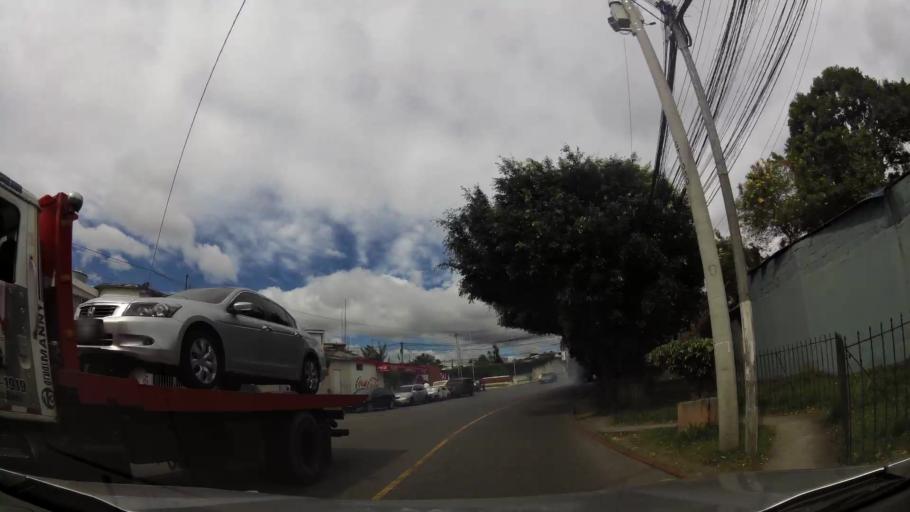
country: GT
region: Guatemala
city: Santa Catarina Pinula
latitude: 14.5853
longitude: -90.5315
